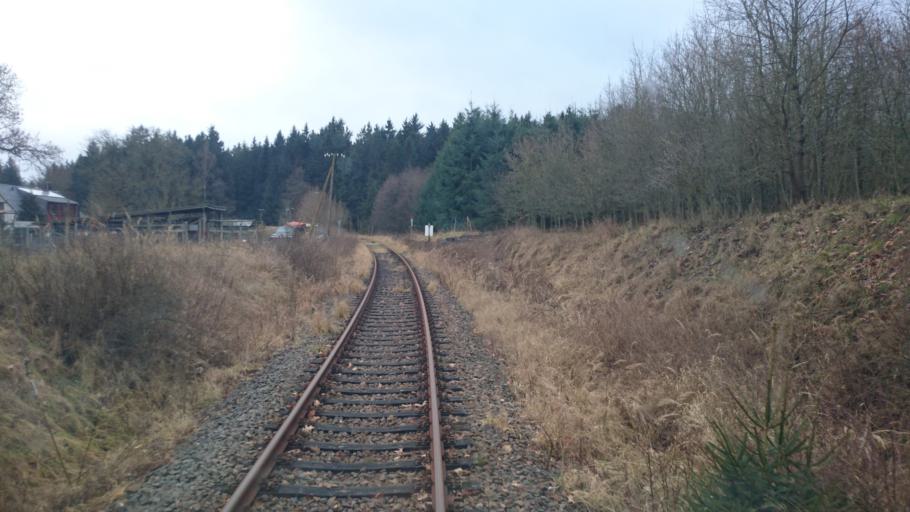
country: DE
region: Thuringia
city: Kirschkau
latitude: 50.5659
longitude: 11.8909
